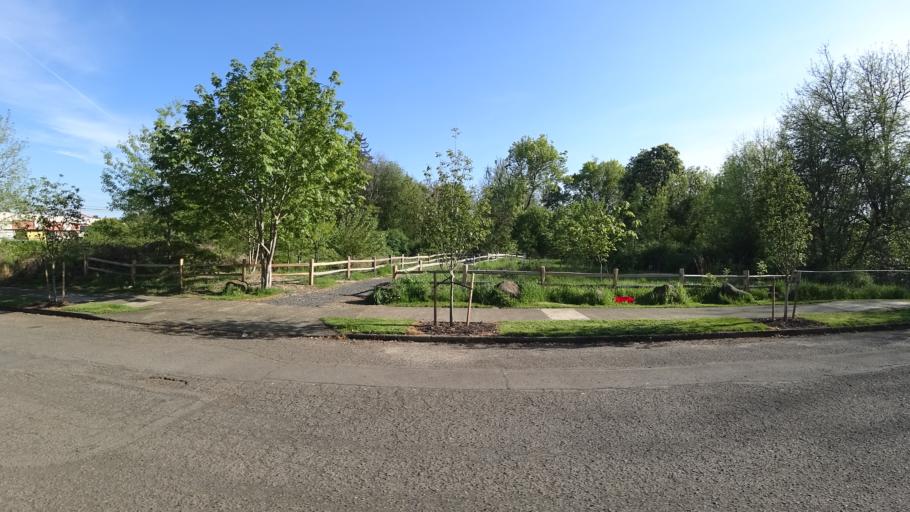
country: US
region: Oregon
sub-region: Clackamas County
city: Milwaukie
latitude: 45.4615
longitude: -122.6419
